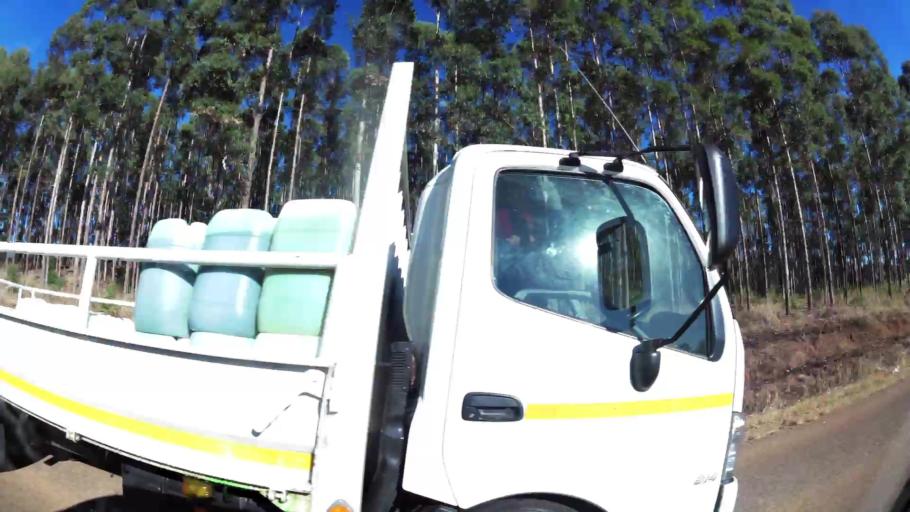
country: ZA
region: Limpopo
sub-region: Mopani District Municipality
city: Tzaneen
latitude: -23.8664
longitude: 30.1081
